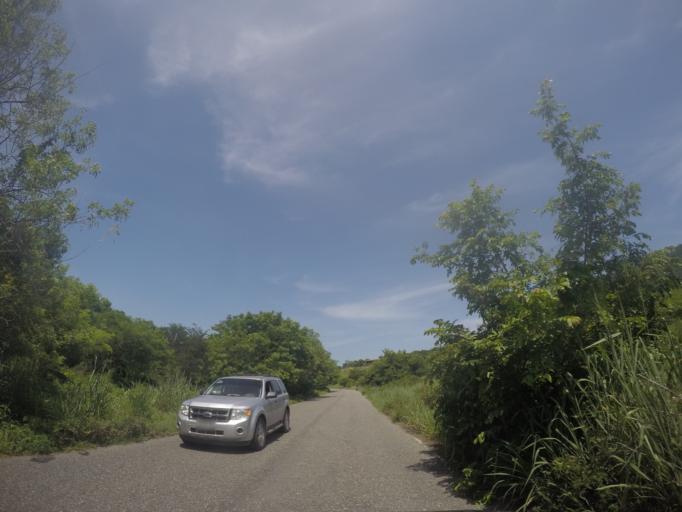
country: MX
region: Oaxaca
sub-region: Villa de Tututepec de Melchor Ocampo
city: Santa Rosa de Lima
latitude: 15.9924
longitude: -97.5368
